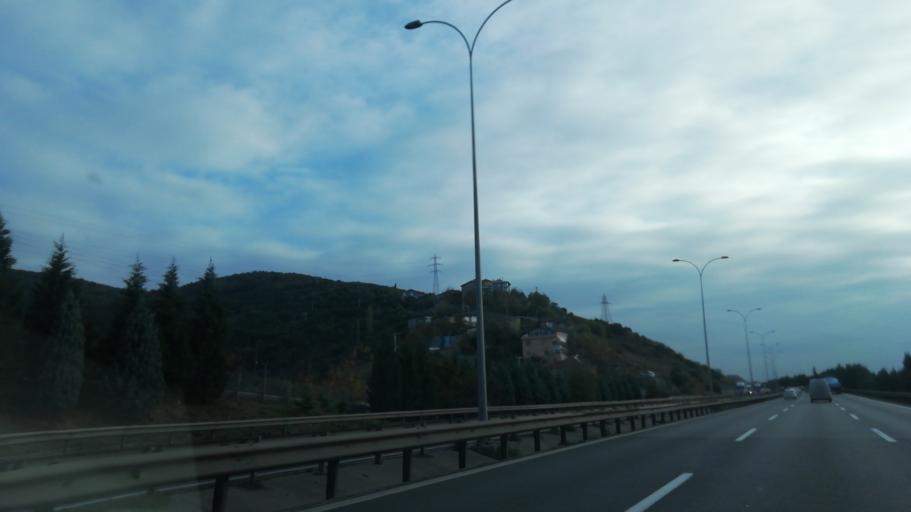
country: TR
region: Kocaeli
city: Ulasli
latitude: 40.7794
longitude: 29.6988
